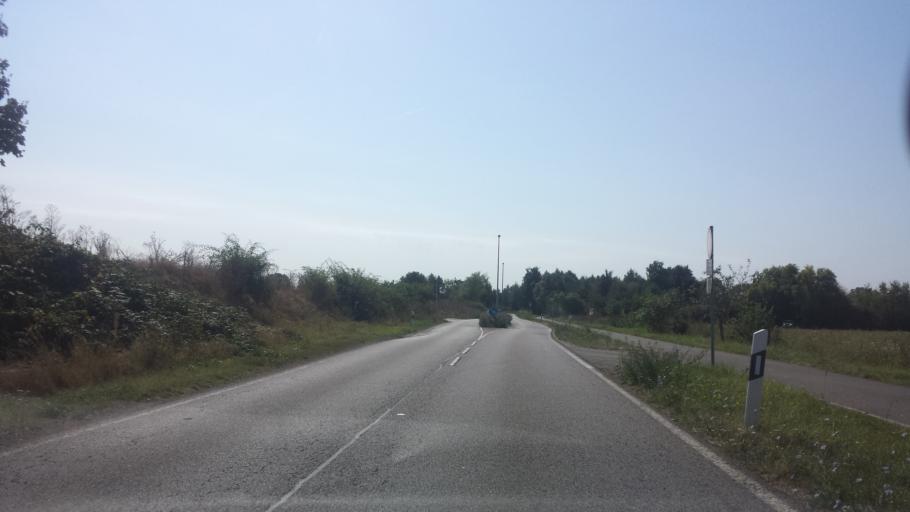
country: DE
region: Rheinland-Pfalz
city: Hassloch
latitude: 49.3563
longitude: 8.2378
